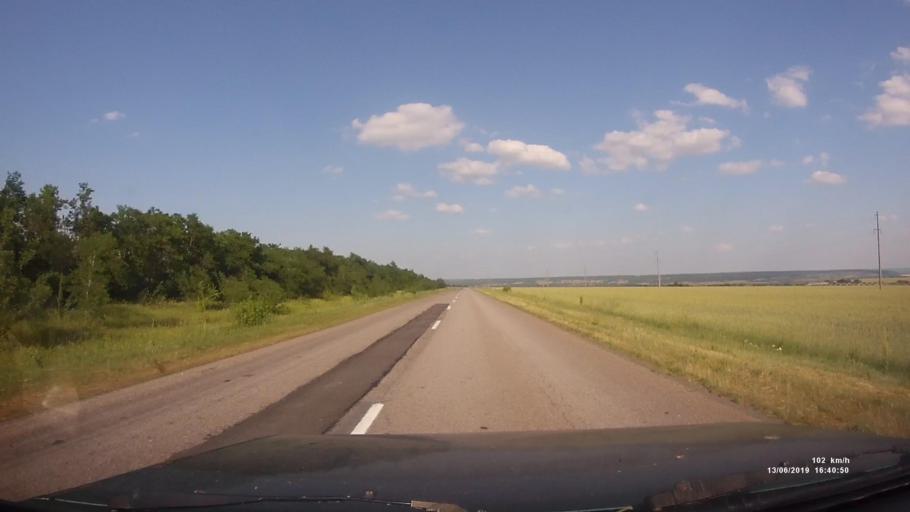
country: RU
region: Rostov
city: Kazanskaya
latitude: 49.9331
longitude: 41.3707
